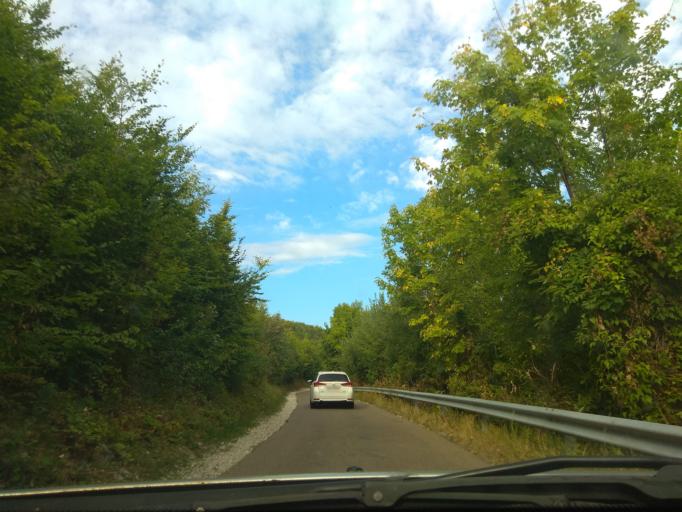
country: HU
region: Borsod-Abauj-Zemplen
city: Saly
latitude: 48.0704
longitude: 20.6589
